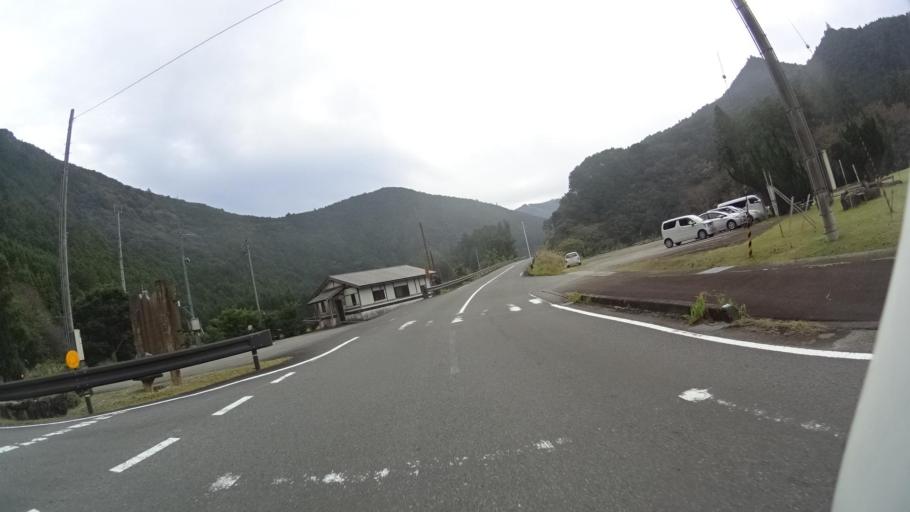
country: JP
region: Wakayama
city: Shingu
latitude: 33.5572
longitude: 135.6922
